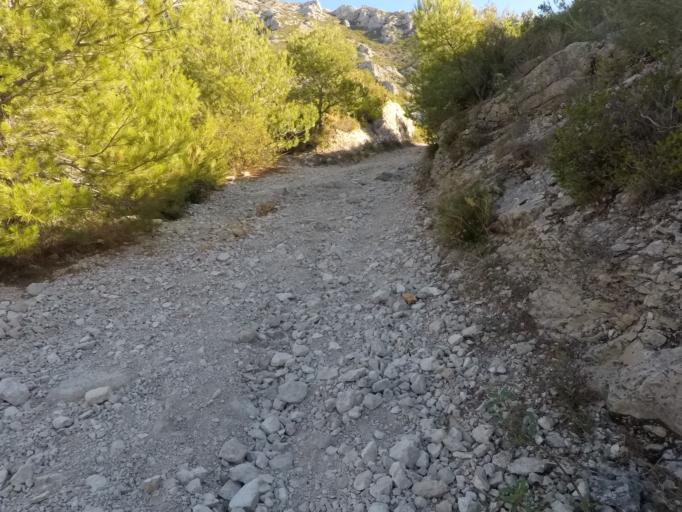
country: FR
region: Provence-Alpes-Cote d'Azur
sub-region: Departement des Bouches-du-Rhone
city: La Penne-sur-Huveaune
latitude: 43.2708
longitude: 5.4871
